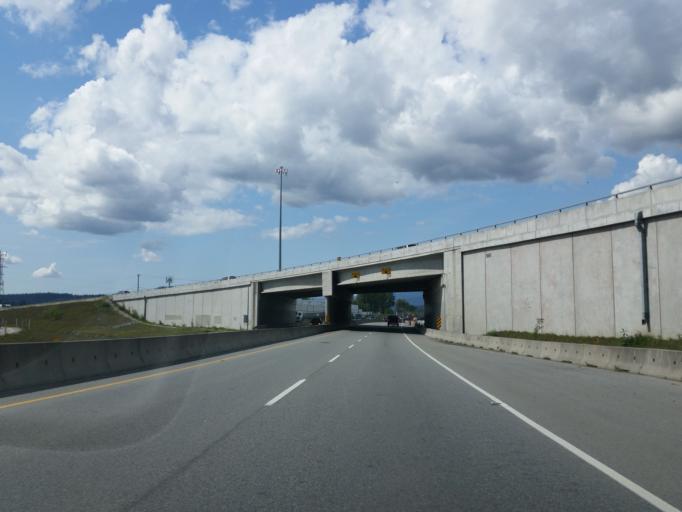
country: CA
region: British Columbia
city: Coquitlam
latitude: 49.2500
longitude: -122.7344
